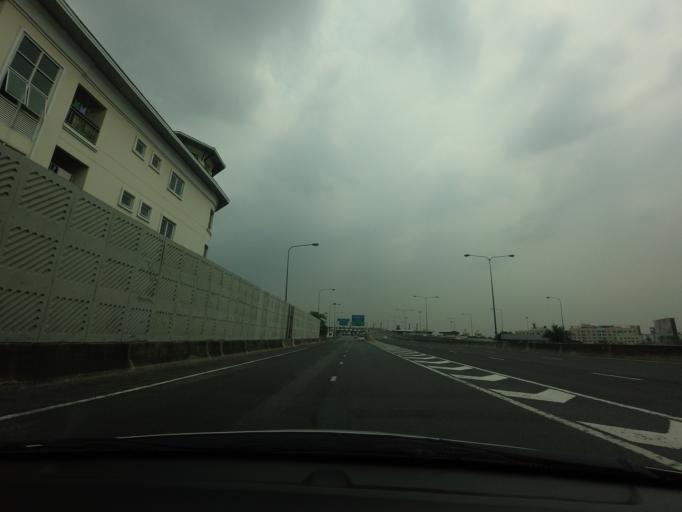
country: TH
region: Bangkok
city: Phra Khanong
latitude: 13.7045
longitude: 100.5939
